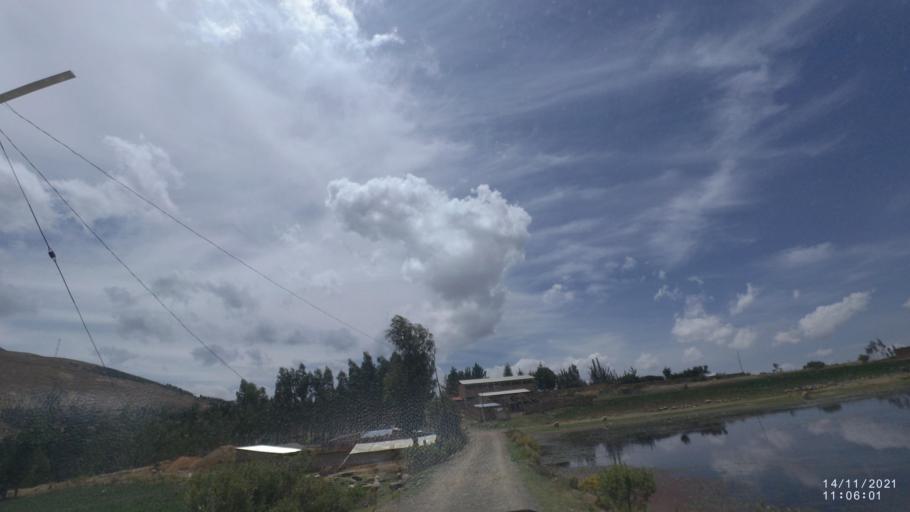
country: BO
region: Cochabamba
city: Cochabamba
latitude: -17.3326
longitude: -66.0557
